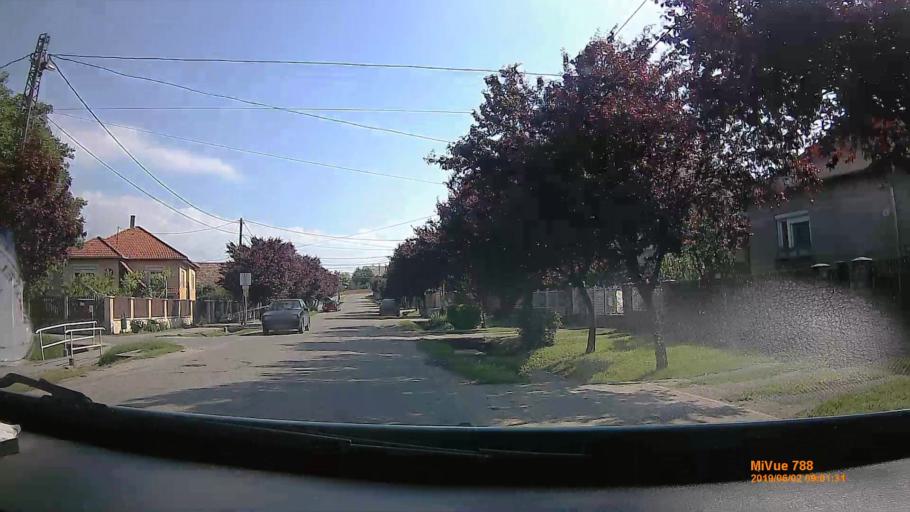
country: HU
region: Borsod-Abauj-Zemplen
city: Kazincbarcika
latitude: 48.1638
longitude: 20.6249
